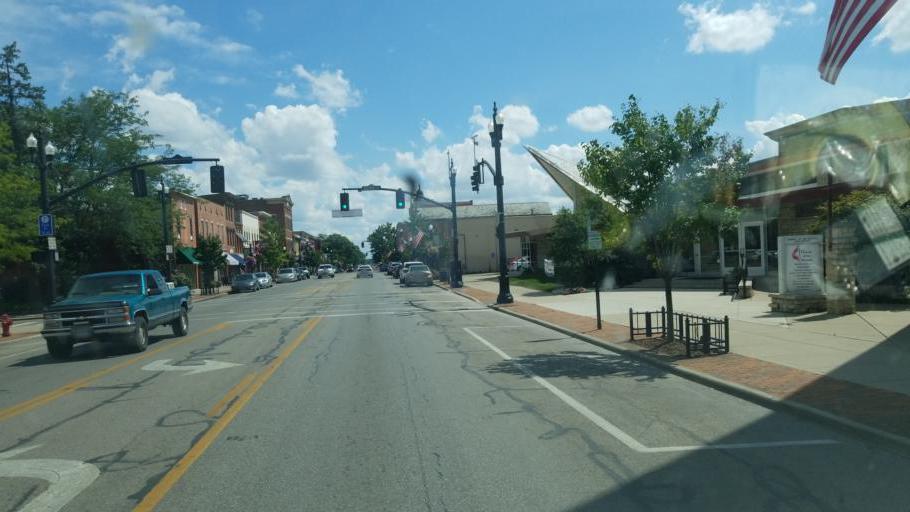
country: US
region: Ohio
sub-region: Franklin County
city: Westerville
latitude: 40.1278
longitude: -82.9323
